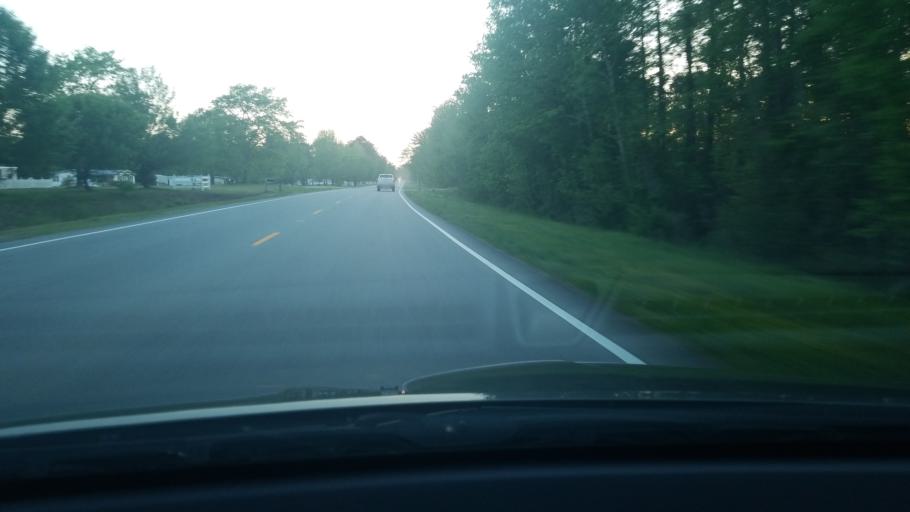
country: US
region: North Carolina
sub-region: Craven County
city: Vanceboro
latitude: 35.2336
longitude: -77.1077
